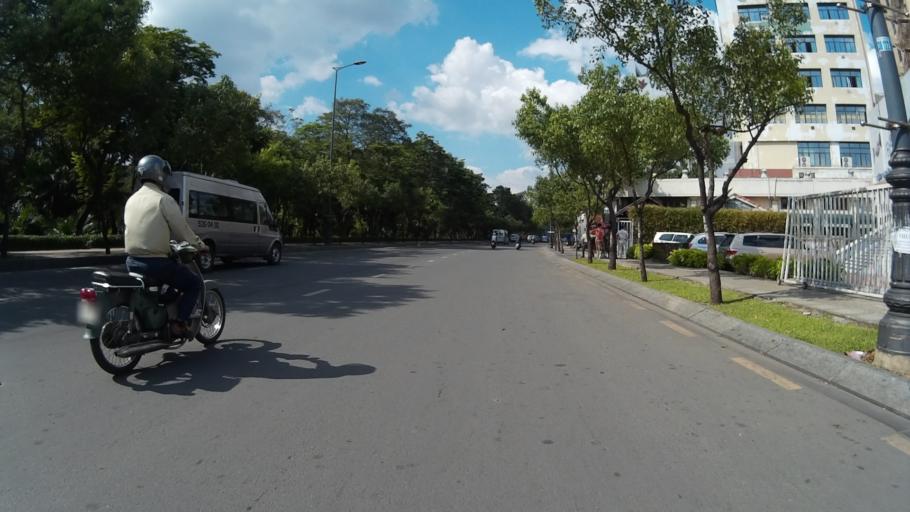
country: VN
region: Ho Chi Minh City
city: Quan Phu Nhuan
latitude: 10.8024
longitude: 106.6653
